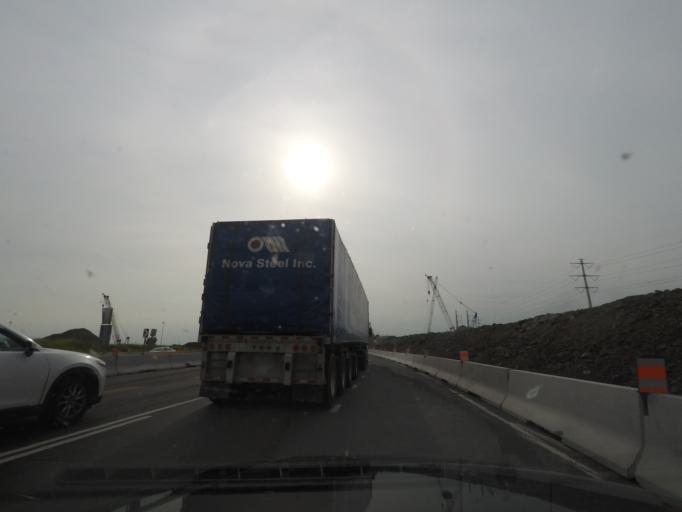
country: CA
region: Quebec
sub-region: Monteregie
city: Brossard
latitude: 45.4662
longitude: -73.4892
